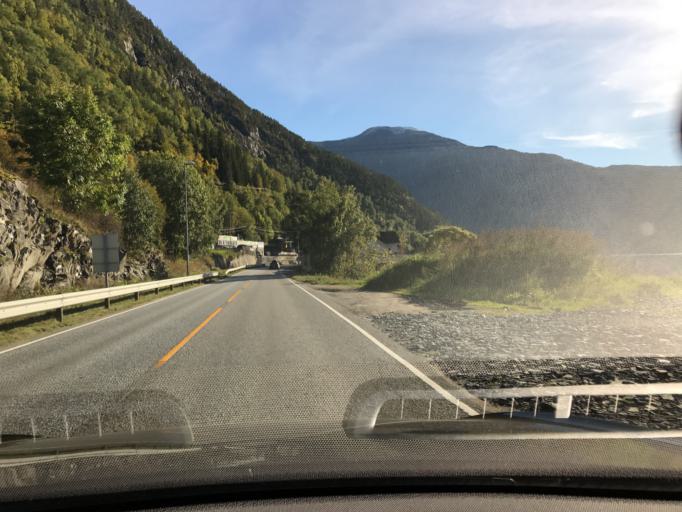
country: NO
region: Sogn og Fjordane
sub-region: Sogndal
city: Sogndalsfjora
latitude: 61.2258
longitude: 7.1256
